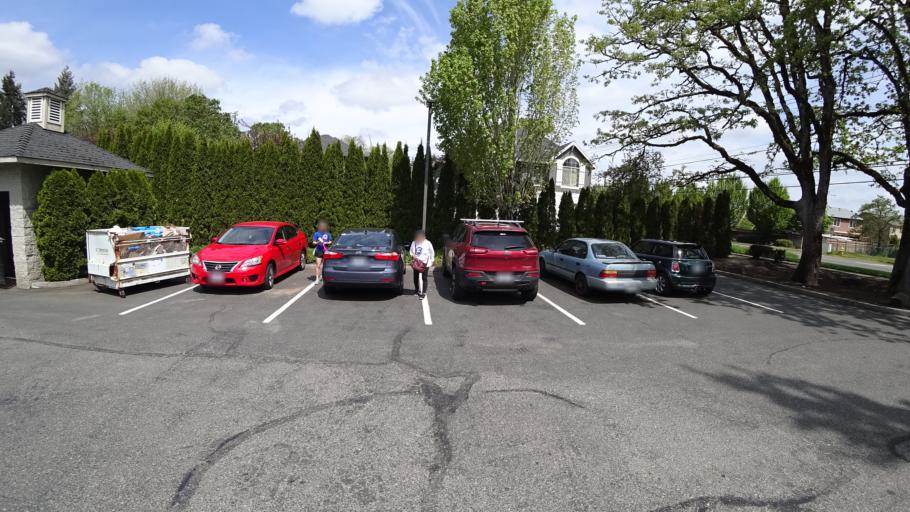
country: US
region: Oregon
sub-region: Washington County
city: Hillsboro
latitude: 45.5431
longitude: -122.9961
